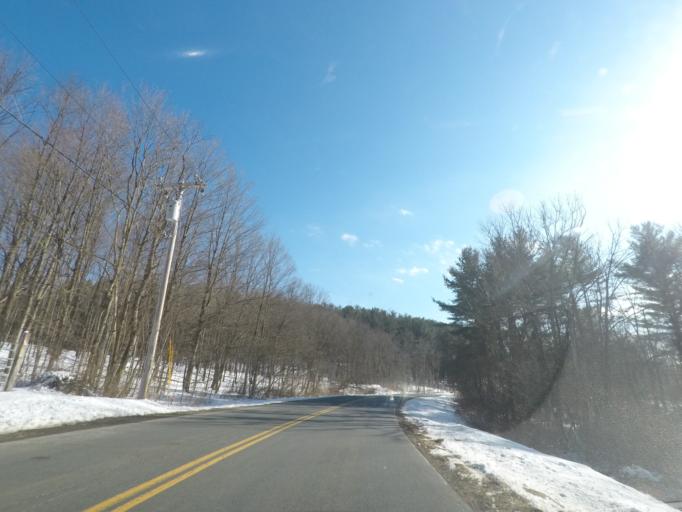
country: US
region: New York
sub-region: Rensselaer County
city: Hoosick Falls
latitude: 42.8908
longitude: -73.4953
